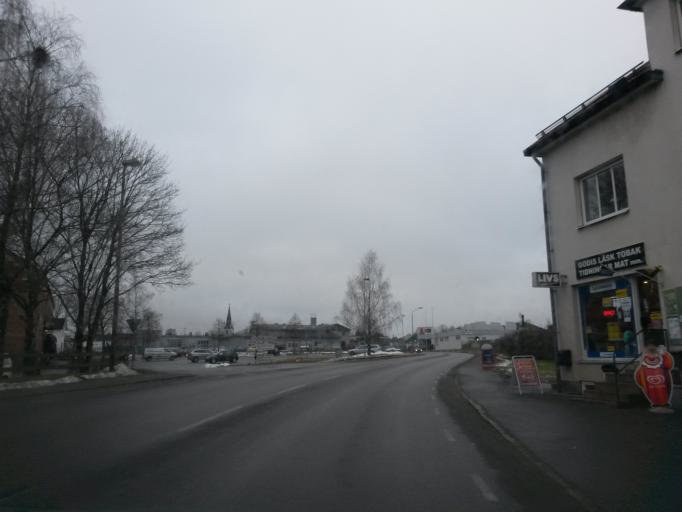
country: SE
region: Vaestra Goetaland
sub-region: Marks Kommun
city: Kinna
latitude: 57.5109
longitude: 12.7034
